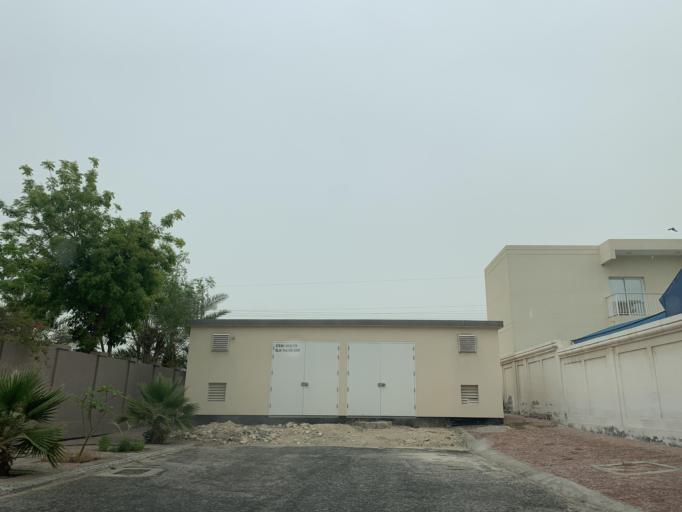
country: BH
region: Northern
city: Ar Rifa'
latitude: 26.1484
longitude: 50.5350
